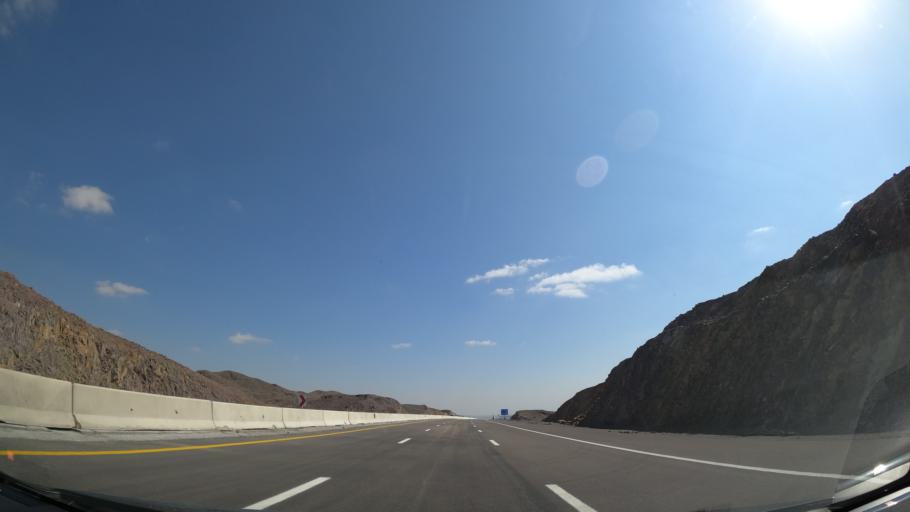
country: IR
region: Alborz
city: Nazarabad
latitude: 35.6591
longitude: 50.6604
